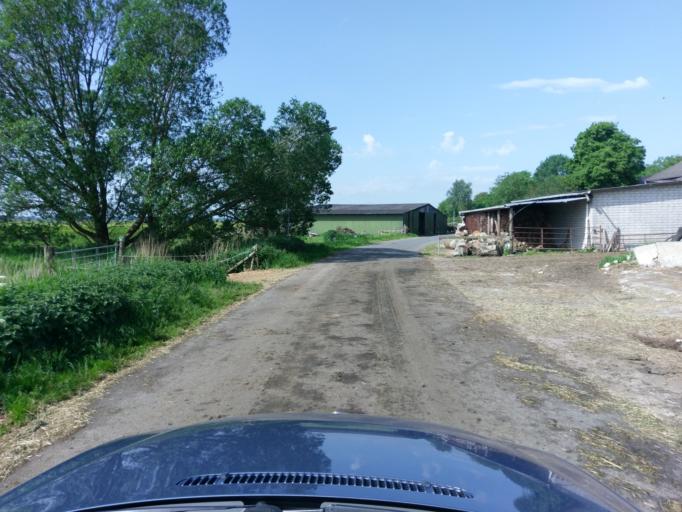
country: DE
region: Schleswig-Holstein
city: Bergewohrden
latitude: 54.3190
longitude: 9.2129
